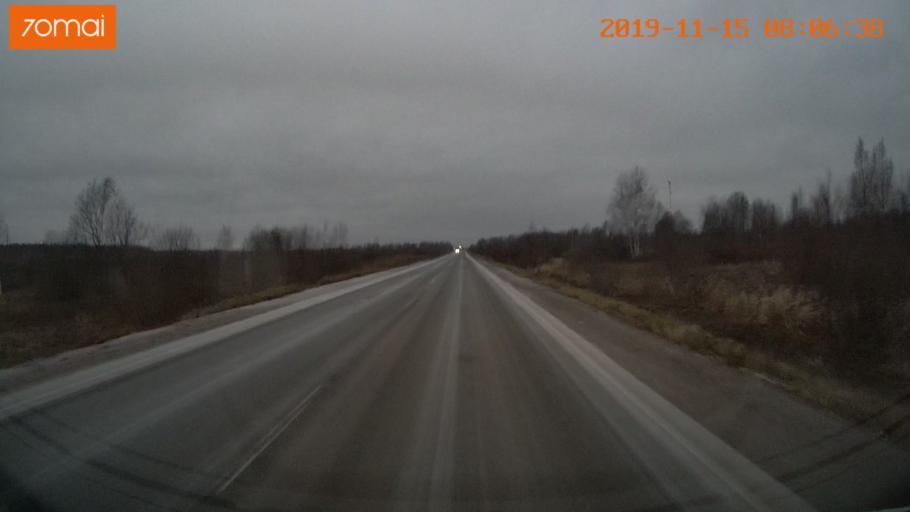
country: RU
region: Vologda
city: Cherepovets
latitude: 59.0232
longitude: 38.0335
